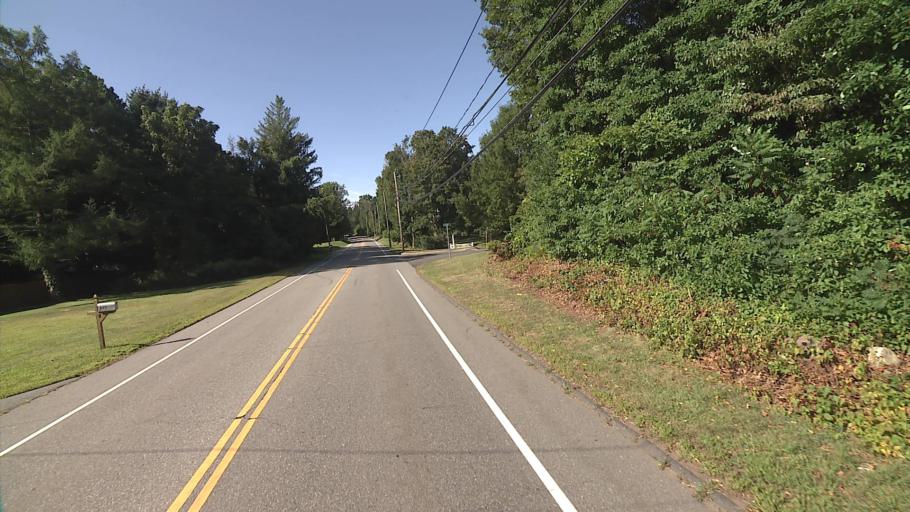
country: US
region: Connecticut
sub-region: New Haven County
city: Cheshire Village
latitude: 41.5191
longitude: -72.8689
